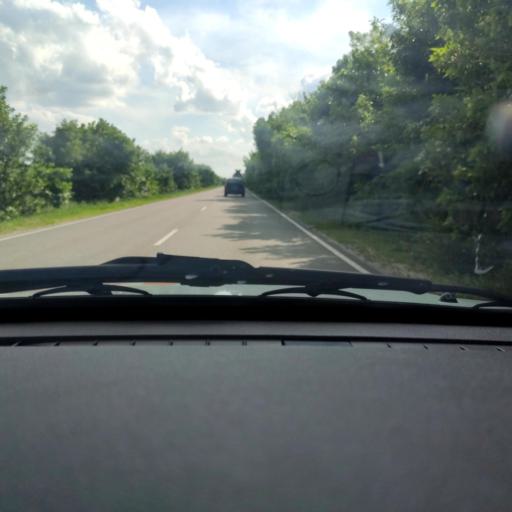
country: RU
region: Voronezj
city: Volya
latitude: 51.6981
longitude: 39.5099
